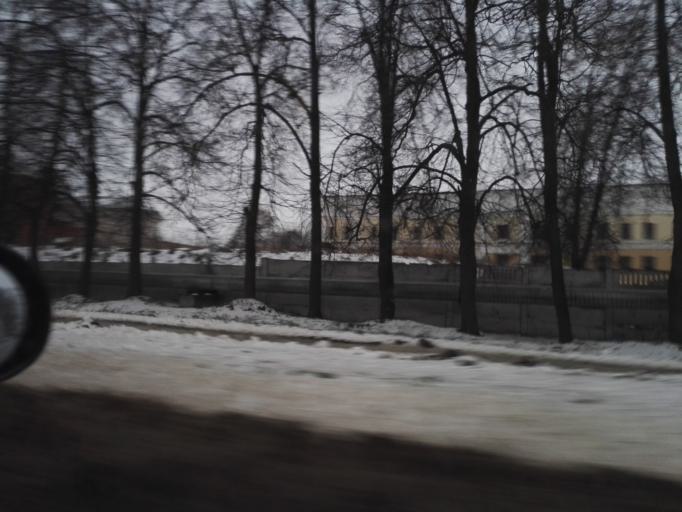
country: RU
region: Tula
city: Novomoskovsk
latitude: 54.0193
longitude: 38.3044
